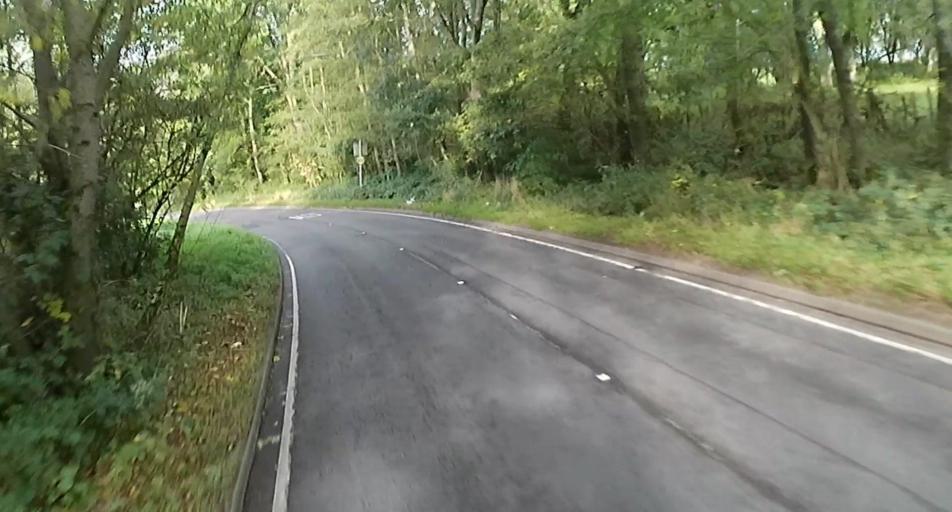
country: GB
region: England
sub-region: West Berkshire
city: Thatcham
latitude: 51.3837
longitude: -1.2487
